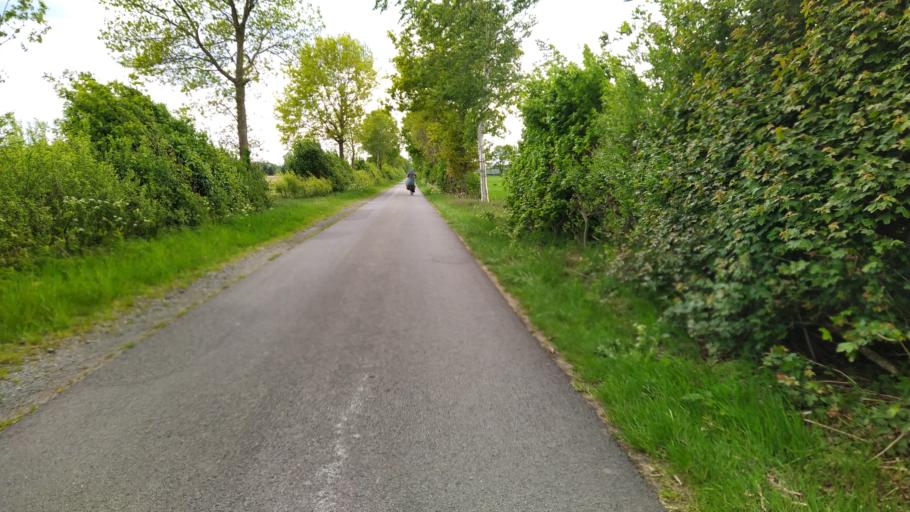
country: DE
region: Lower Saxony
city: Ahlerstedt
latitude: 53.3855
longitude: 9.4004
